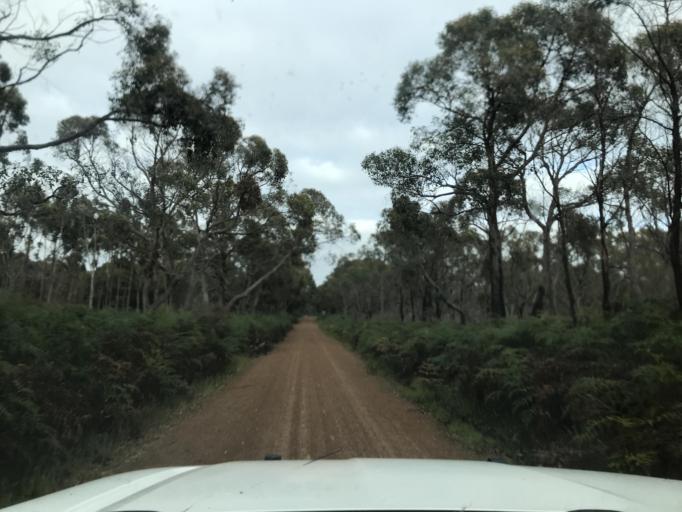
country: AU
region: South Australia
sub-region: Wattle Range
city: Penola
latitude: -37.2795
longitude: 141.3852
